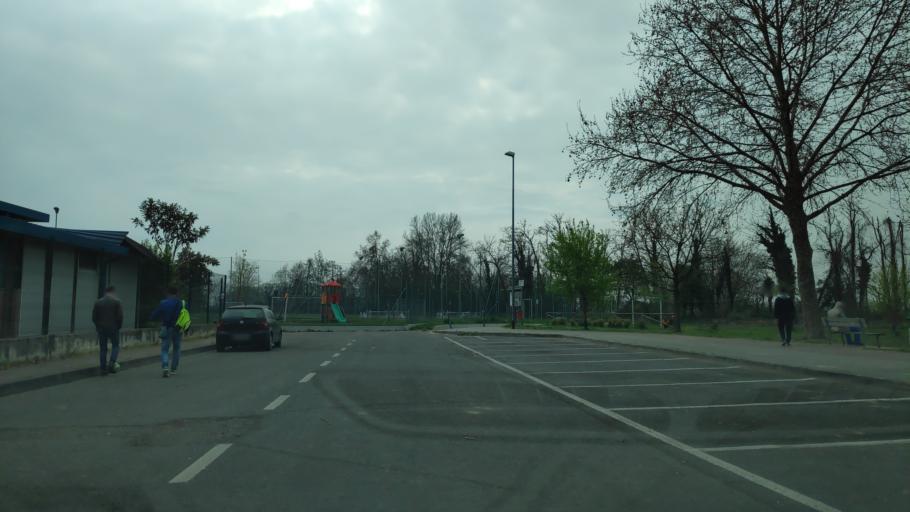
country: IT
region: Lombardy
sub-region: Citta metropolitana di Milano
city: Liscate
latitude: 45.4778
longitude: 9.4076
